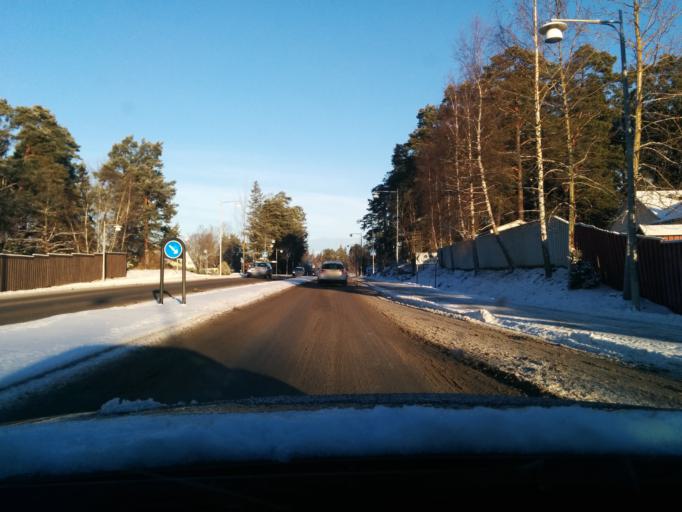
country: SE
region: Stockholm
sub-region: Vallentuna Kommun
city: Vallentuna
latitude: 59.4959
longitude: 18.0616
